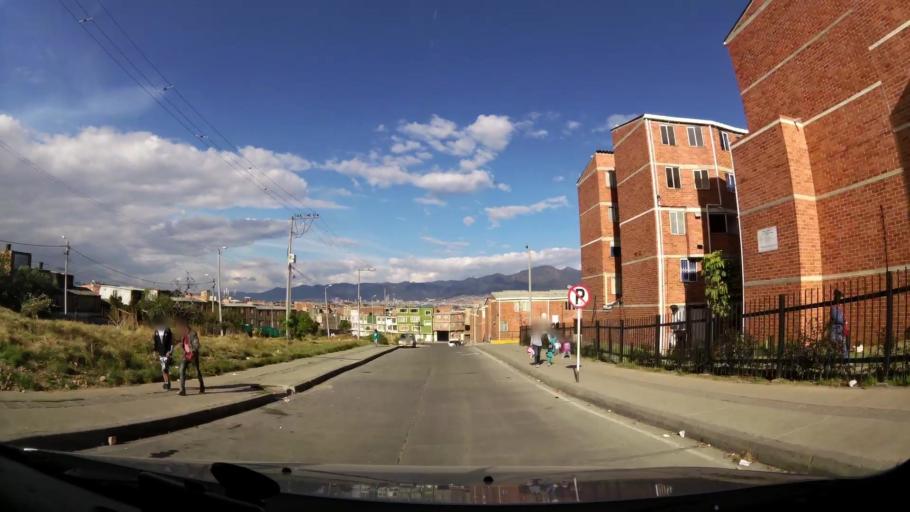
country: CO
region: Cundinamarca
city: Soacha
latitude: 4.5680
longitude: -74.1522
